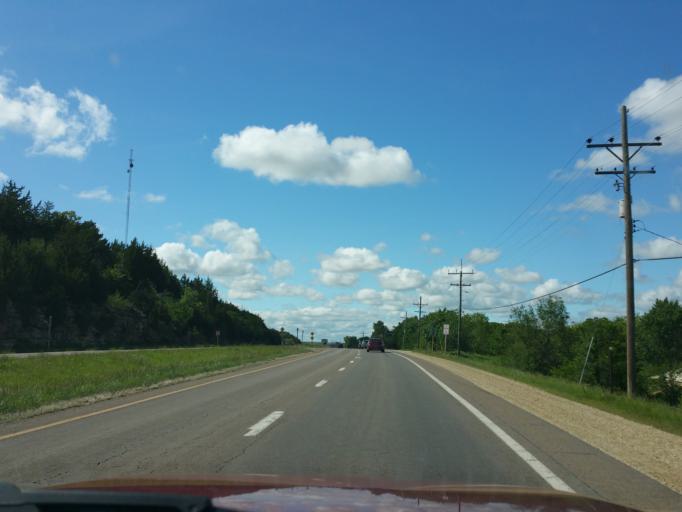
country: US
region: Kansas
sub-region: Riley County
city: Manhattan
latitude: 39.2339
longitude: -96.5870
